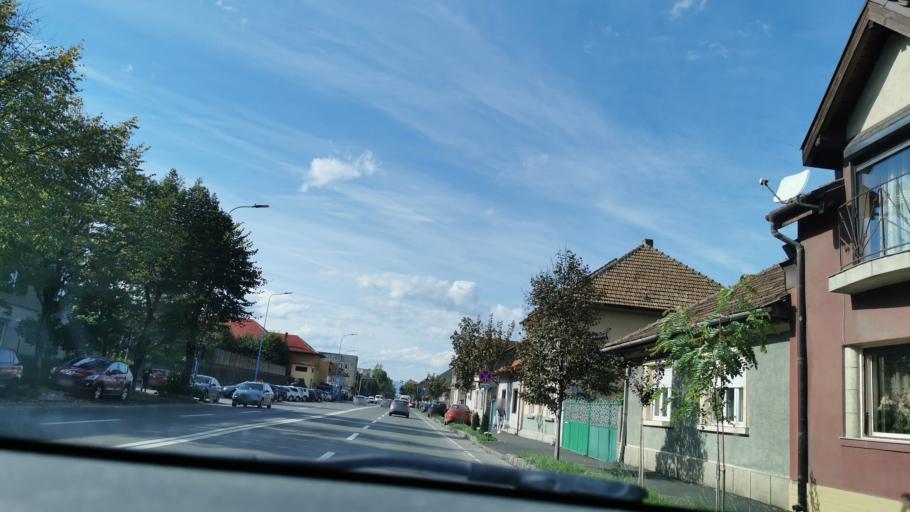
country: RO
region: Brasov
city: Brasov
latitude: 45.6659
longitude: 25.6069
